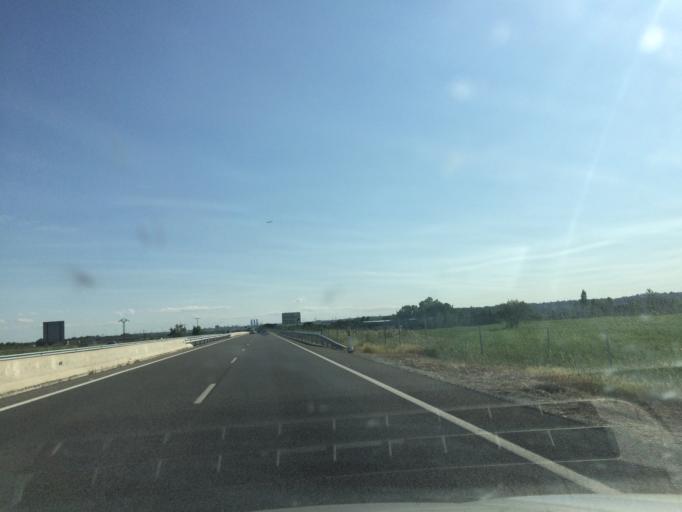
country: ES
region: Madrid
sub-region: Provincia de Madrid
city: Fuente el Saz
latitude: 40.6013
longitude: -3.5553
